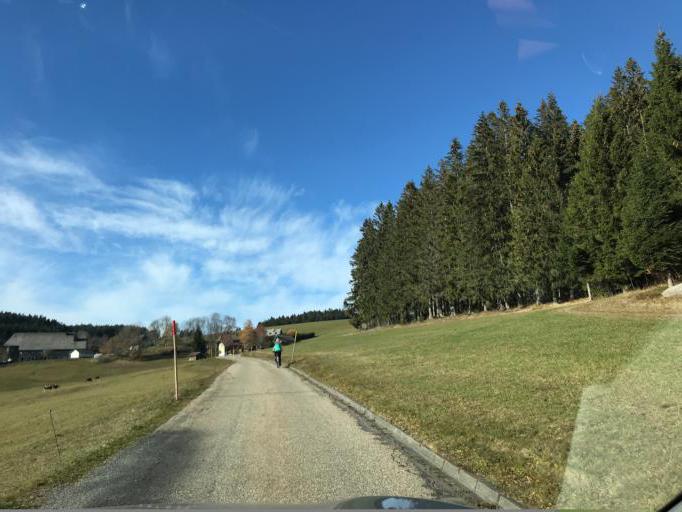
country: DE
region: Baden-Wuerttemberg
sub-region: Freiburg Region
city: Schonwald im Schwarzwald
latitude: 48.0919
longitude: 8.1663
